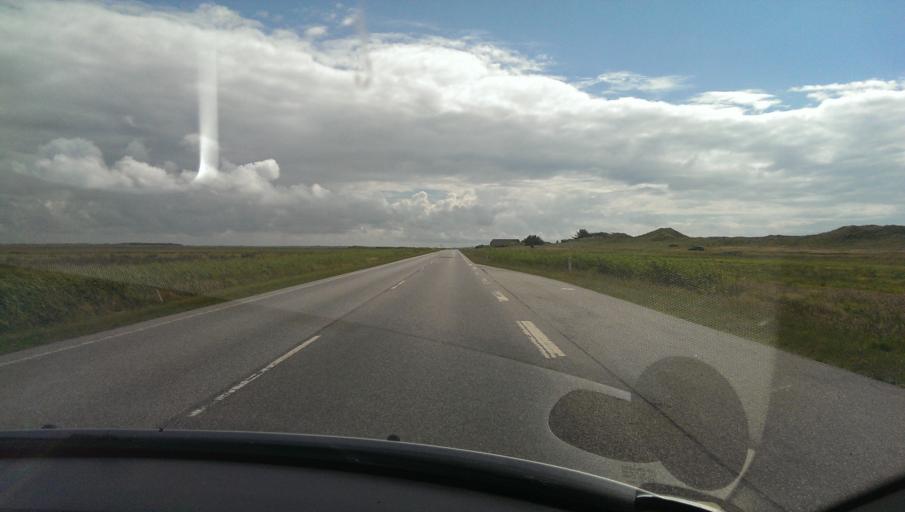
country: DK
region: Central Jutland
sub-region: Ringkobing-Skjern Kommune
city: Ringkobing
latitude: 56.2221
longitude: 8.1396
